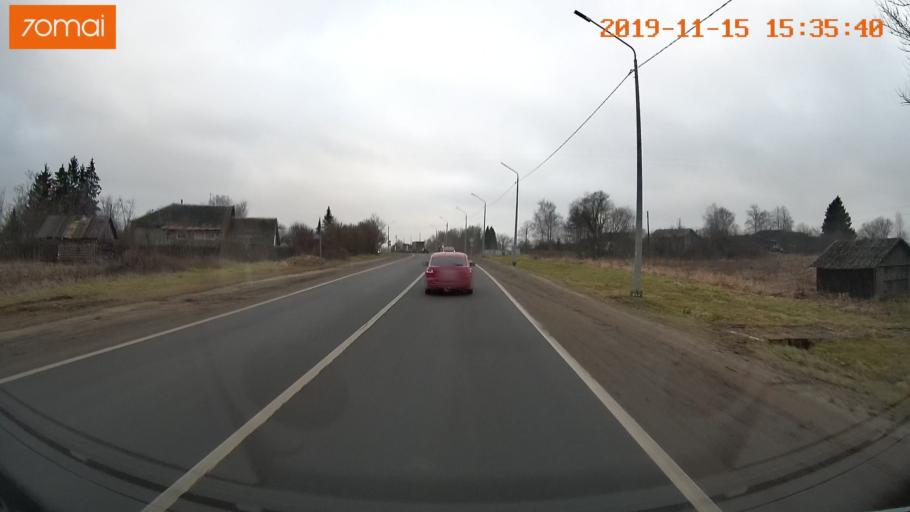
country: RU
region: Jaroslavl
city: Danilov
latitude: 58.0566
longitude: 40.0876
